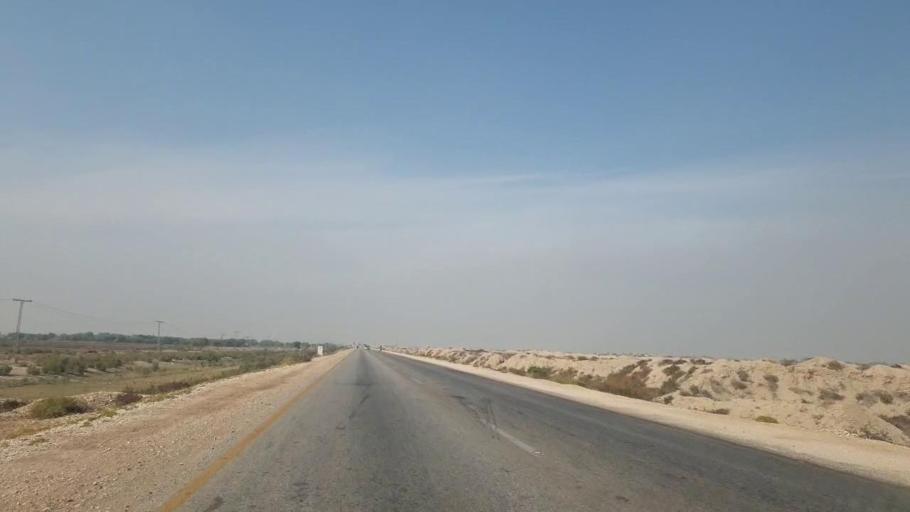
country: PK
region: Sindh
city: Sann
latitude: 25.9352
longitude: 68.2071
